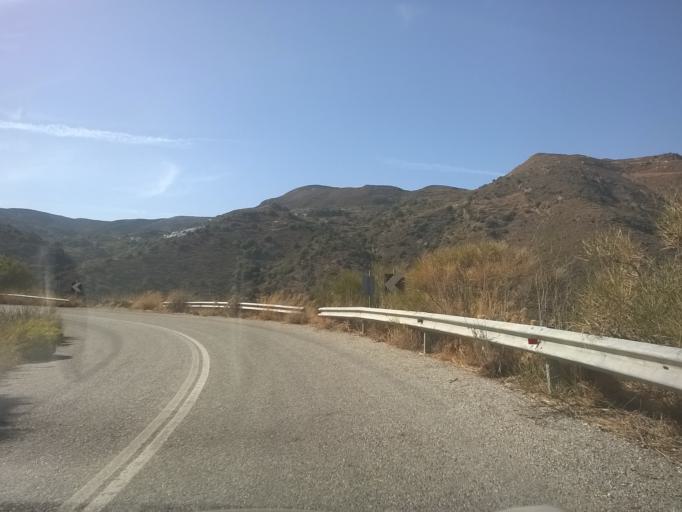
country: GR
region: South Aegean
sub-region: Nomos Kykladon
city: Filotion
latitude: 37.1459
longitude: 25.5451
